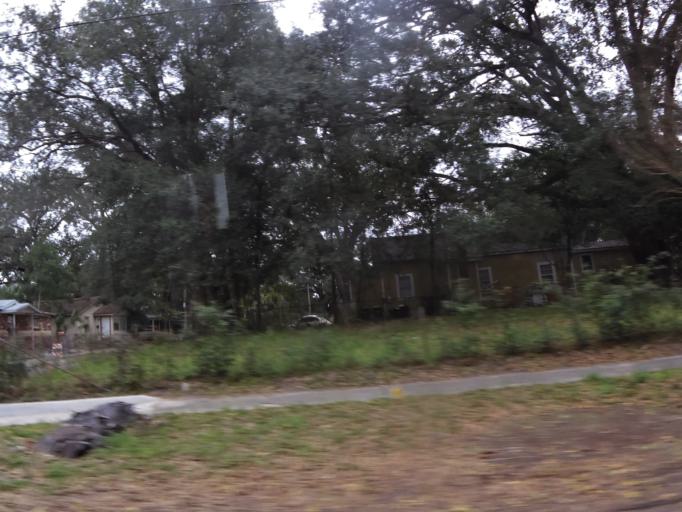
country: US
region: Florida
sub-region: Duval County
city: Jacksonville
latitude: 30.3662
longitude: -81.6849
